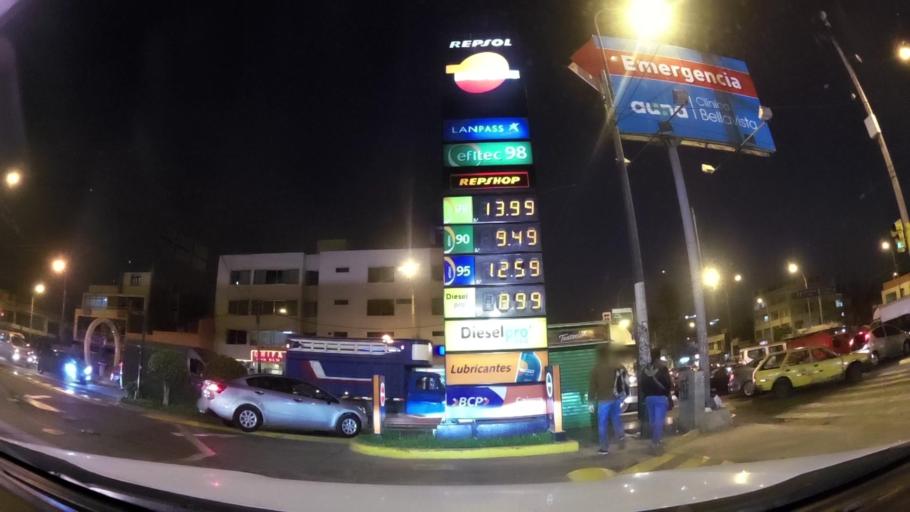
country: PE
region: Callao
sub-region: Callao
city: Callao
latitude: -12.0534
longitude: -77.0956
